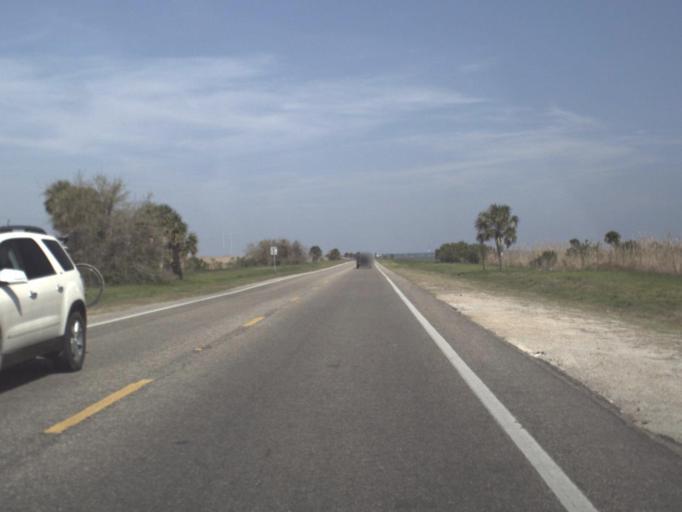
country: US
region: Florida
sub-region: Franklin County
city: Apalachicola
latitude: 29.7261
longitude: -84.9710
